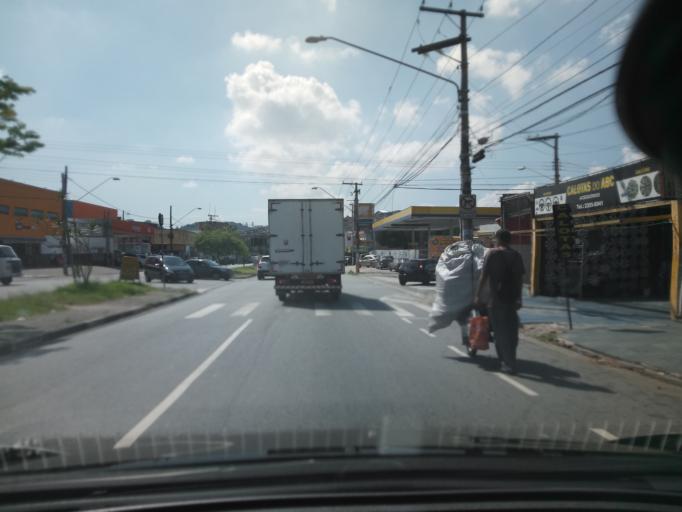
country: BR
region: Sao Paulo
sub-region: Sao Bernardo Do Campo
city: Sao Bernardo do Campo
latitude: -23.7142
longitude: -46.5319
